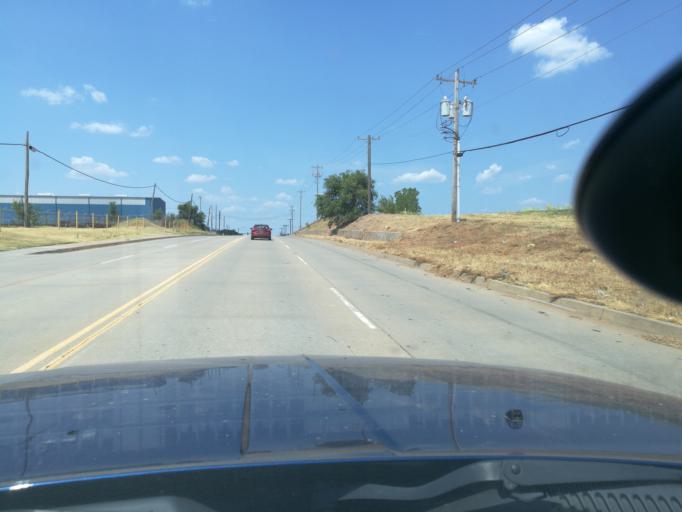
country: US
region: Oklahoma
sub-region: Oklahoma County
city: Del City
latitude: 35.4178
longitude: -97.4770
